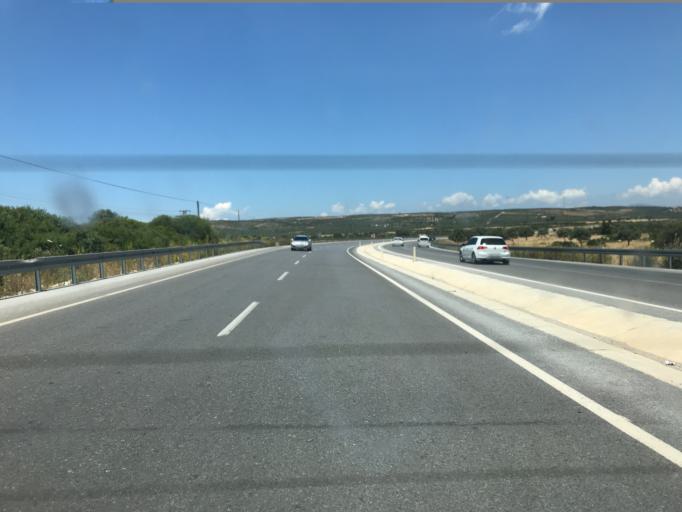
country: TR
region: Aydin
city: Akkoy
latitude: 37.4571
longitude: 27.3411
